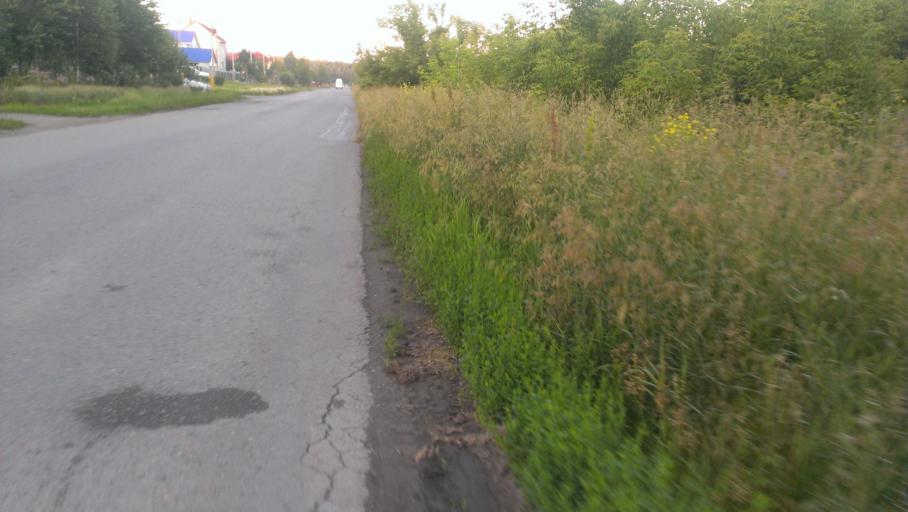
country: RU
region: Altai Krai
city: Novosilikatnyy
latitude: 53.3646
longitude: 83.6480
